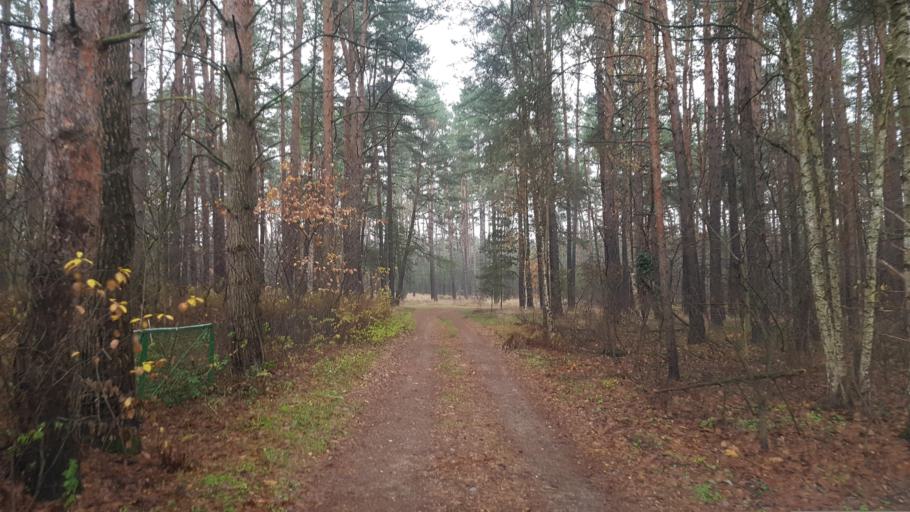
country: DE
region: Brandenburg
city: Sallgast
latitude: 51.6422
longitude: 13.7881
